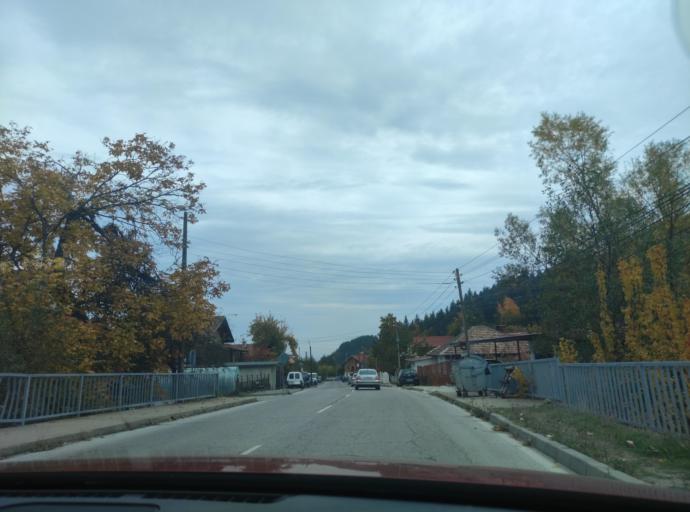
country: BG
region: Montana
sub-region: Obshtina Berkovitsa
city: Berkovitsa
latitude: 43.1905
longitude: 23.1593
